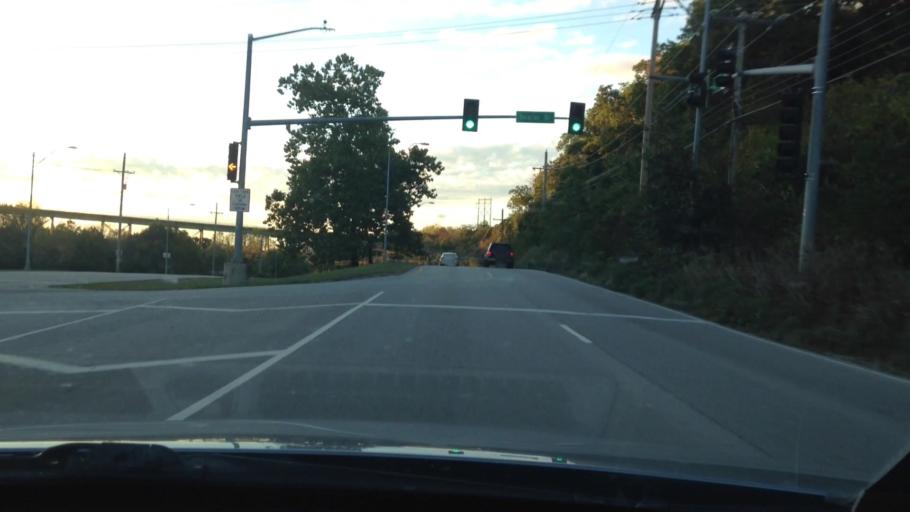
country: US
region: Missouri
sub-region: Jackson County
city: Raytown
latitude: 39.0136
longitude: -94.5107
